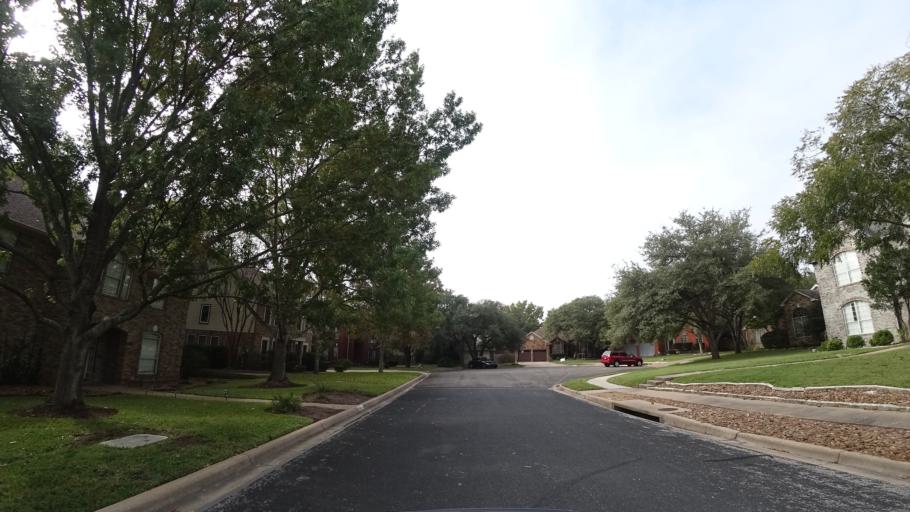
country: US
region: Texas
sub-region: Travis County
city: Shady Hollow
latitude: 30.1938
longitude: -97.8892
